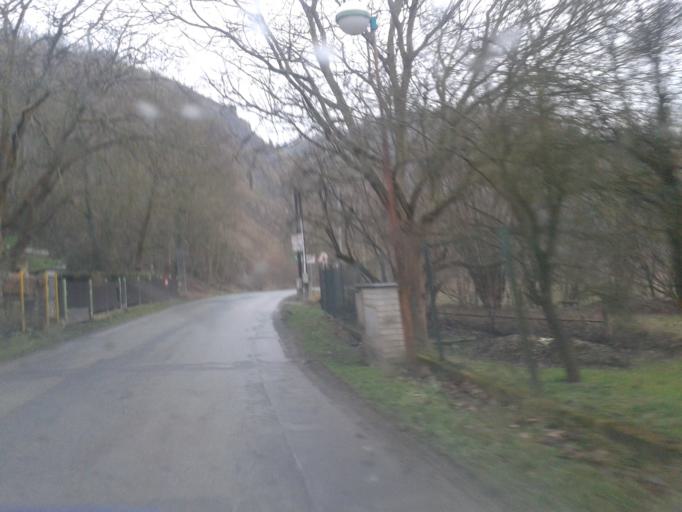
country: CZ
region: Central Bohemia
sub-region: Okres Beroun
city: Lodenice
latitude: 49.9346
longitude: 14.1361
